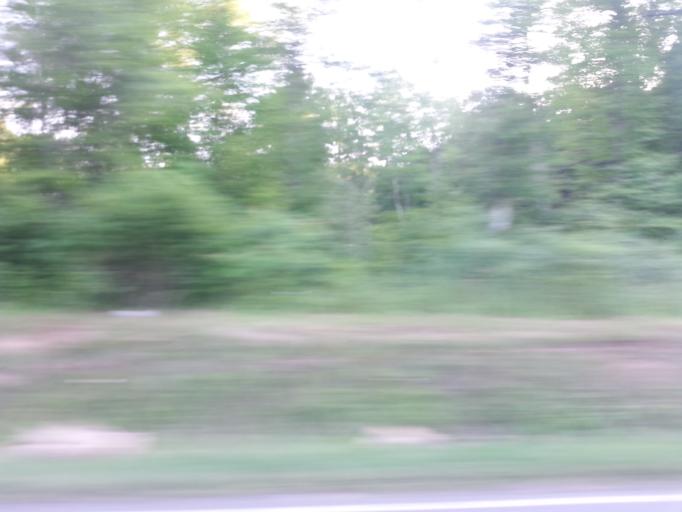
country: US
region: North Carolina
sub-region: Cherokee County
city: Murphy
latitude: 35.0401
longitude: -84.1450
